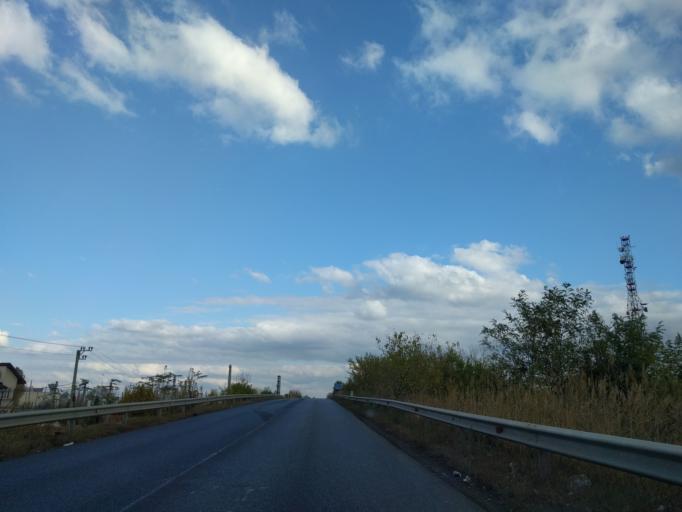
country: RO
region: Ilfov
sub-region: Comuna Pantelimon
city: Pantelimon
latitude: 44.4509
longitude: 26.2335
